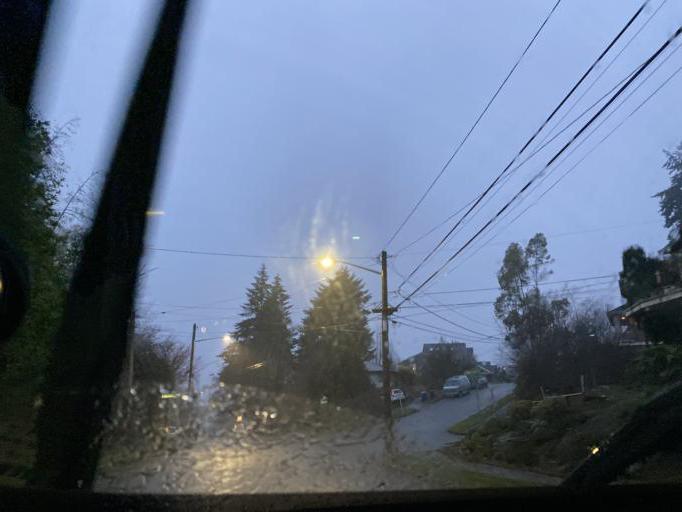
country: US
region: Washington
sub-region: King County
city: Seattle
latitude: 47.6580
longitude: -122.3963
